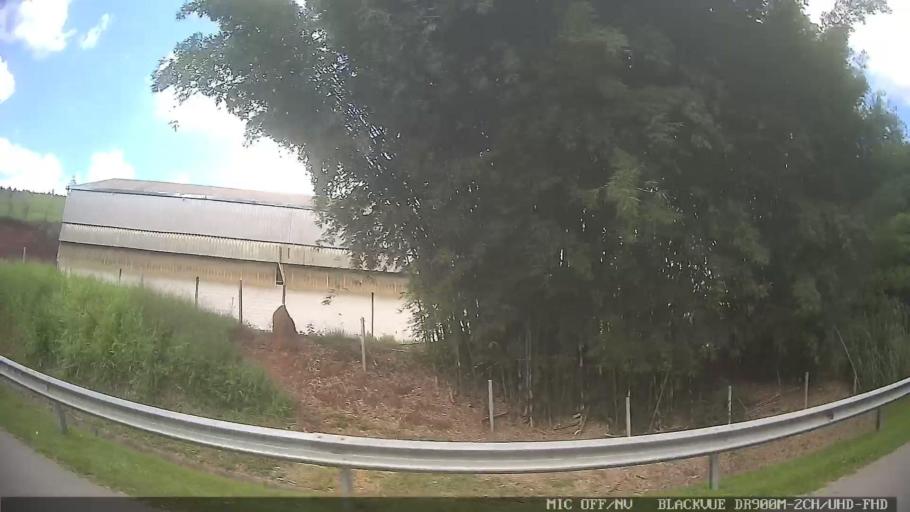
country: BR
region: Sao Paulo
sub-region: Santa Branca
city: Santa Branca
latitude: -23.2912
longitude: -45.7878
